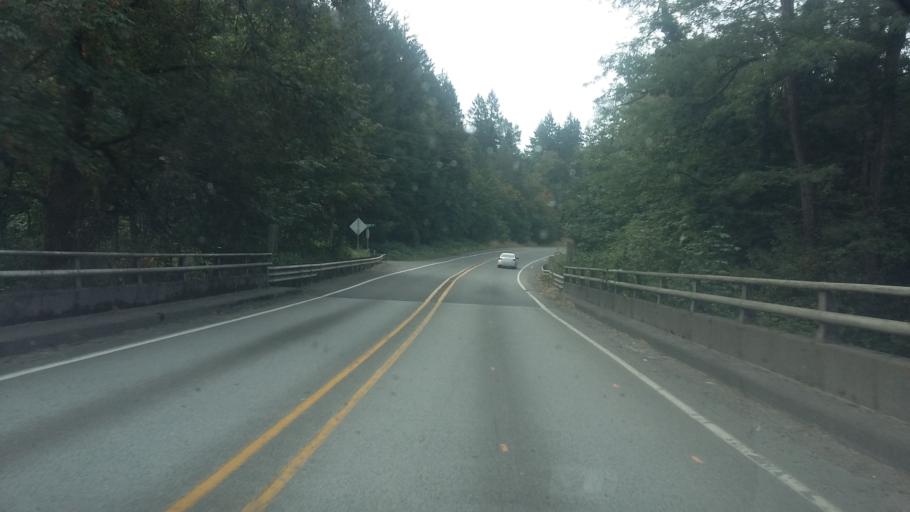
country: US
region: Washington
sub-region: Clark County
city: Lewisville
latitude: 45.8100
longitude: -122.5471
